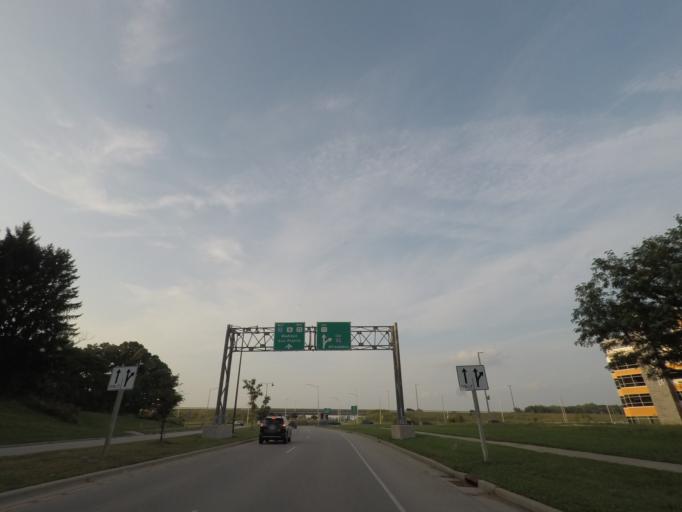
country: US
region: Wisconsin
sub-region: Dane County
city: Cottage Grove
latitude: 43.1074
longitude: -89.1992
